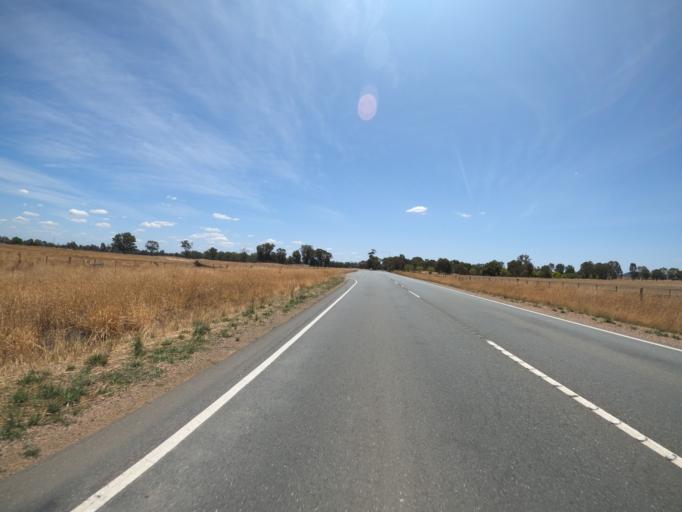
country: AU
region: Victoria
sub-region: Benalla
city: Benalla
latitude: -36.4991
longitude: 146.0211
